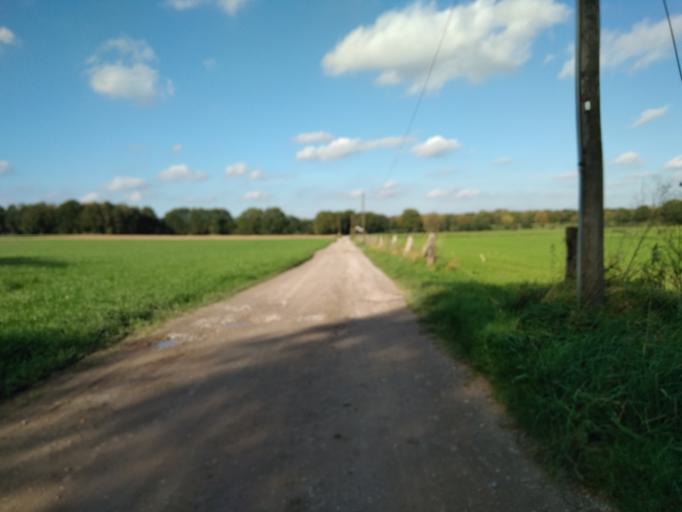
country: DE
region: North Rhine-Westphalia
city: Dorsten
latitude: 51.6260
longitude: 6.9200
